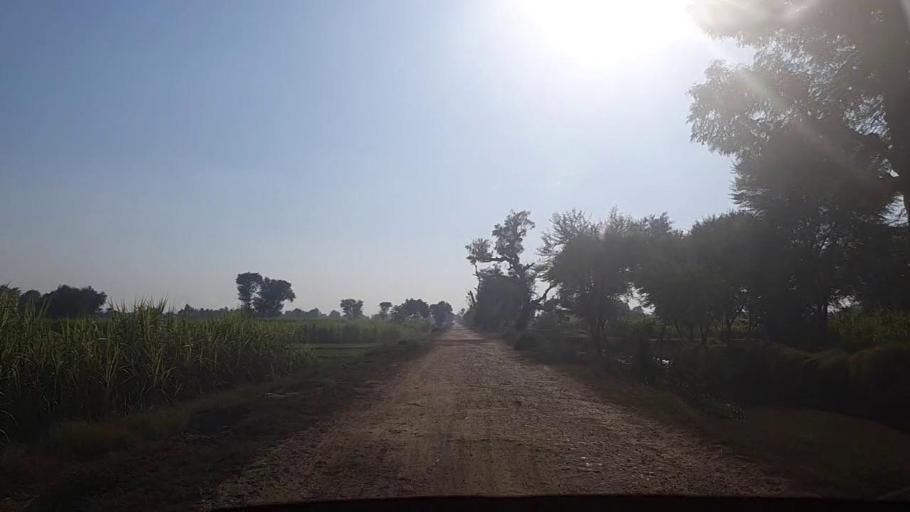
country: PK
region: Sindh
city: Gambat
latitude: 27.3726
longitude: 68.4647
